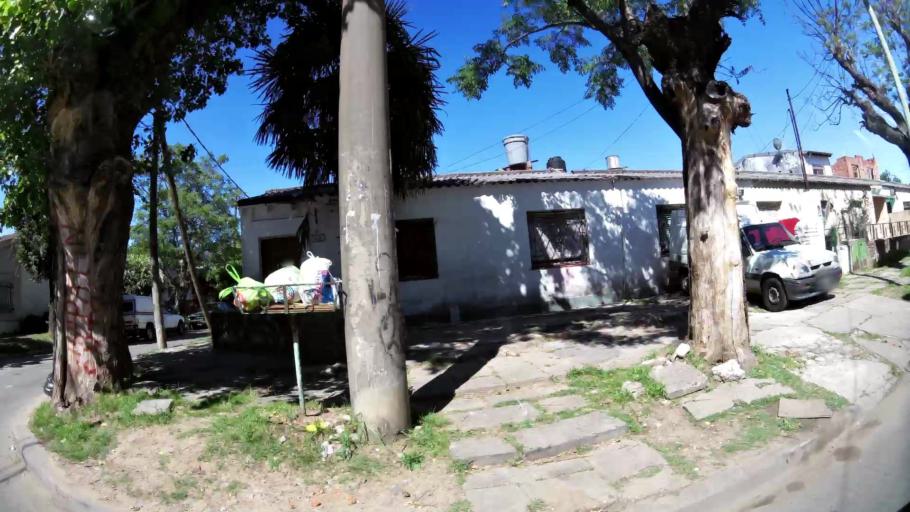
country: AR
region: Buenos Aires
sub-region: Partido de General San Martin
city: General San Martin
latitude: -34.5437
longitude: -58.5304
